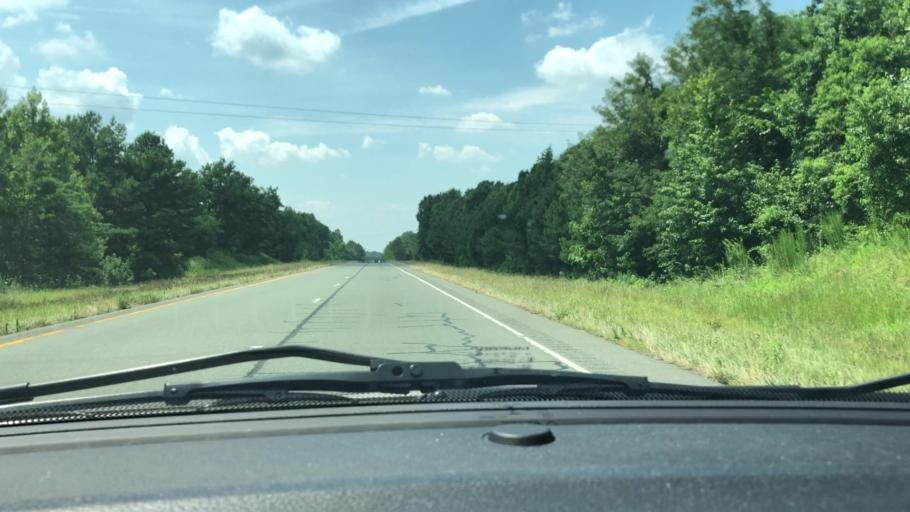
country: US
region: North Carolina
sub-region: Chatham County
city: Siler City
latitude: 35.7751
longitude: -79.4956
